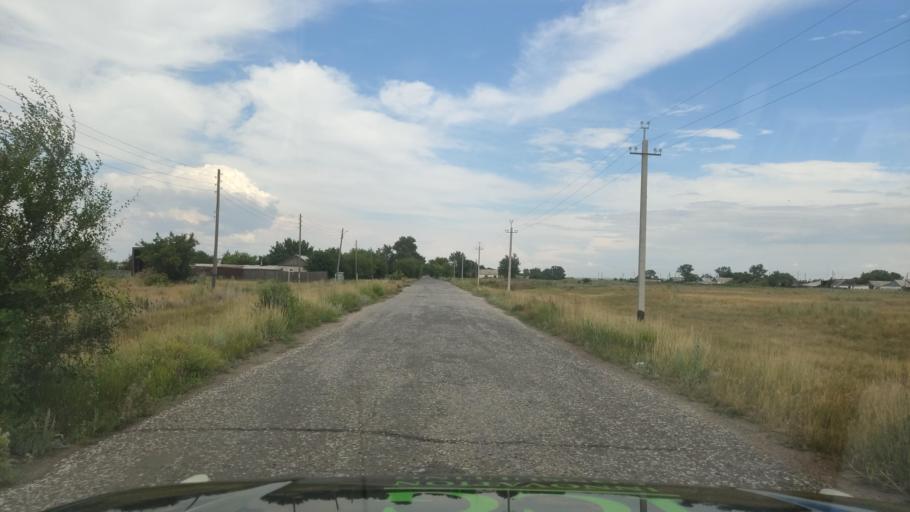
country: KZ
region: Pavlodar
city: Pavlodar
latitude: 52.6614
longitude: 77.5004
